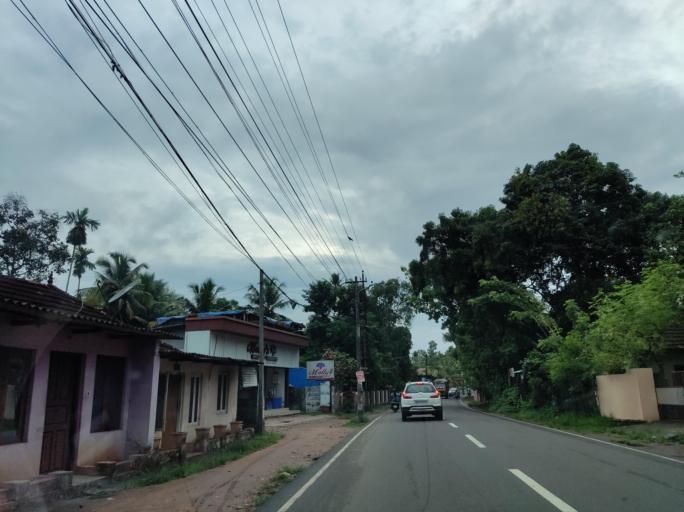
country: IN
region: Kerala
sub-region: Alappuzha
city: Mavelikara
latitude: 9.2518
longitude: 76.5087
